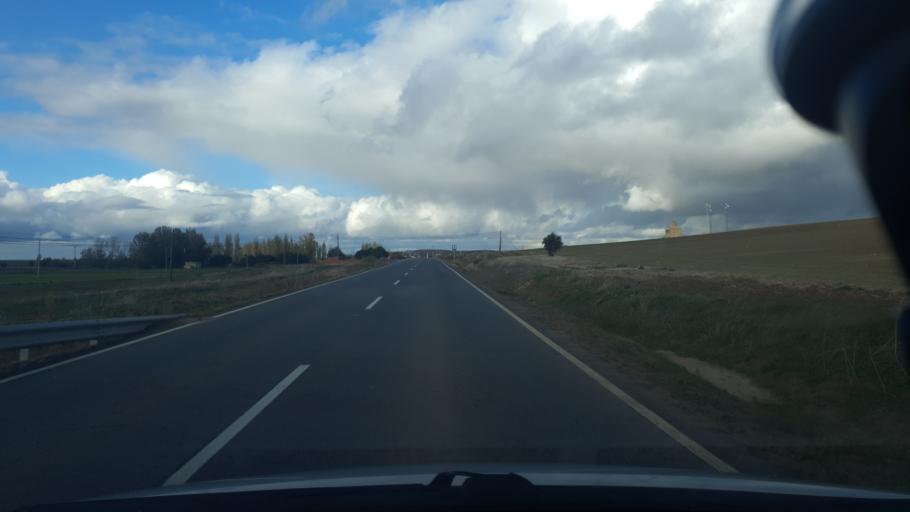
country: ES
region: Castille and Leon
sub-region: Provincia de Avila
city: Hernansancho
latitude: 40.8493
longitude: -4.7298
